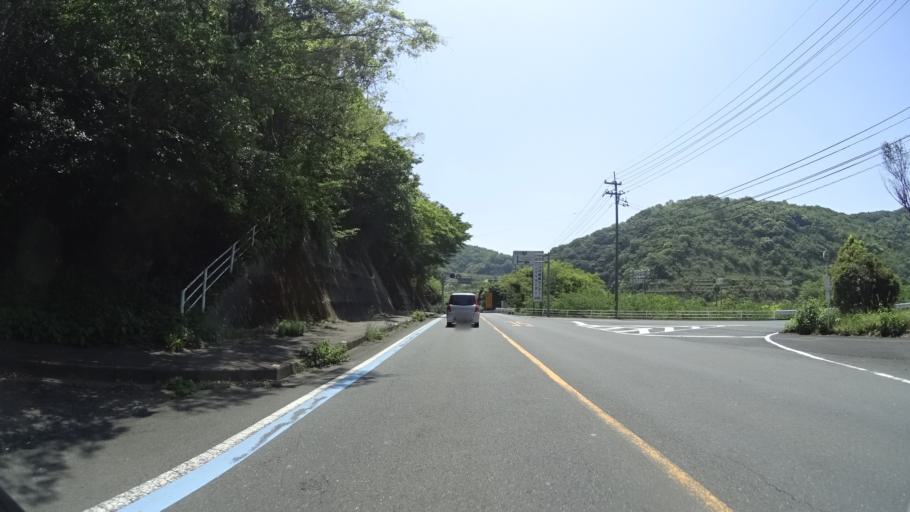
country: JP
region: Ehime
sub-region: Nishiuwa-gun
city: Ikata-cho
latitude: 33.4821
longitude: 132.3263
